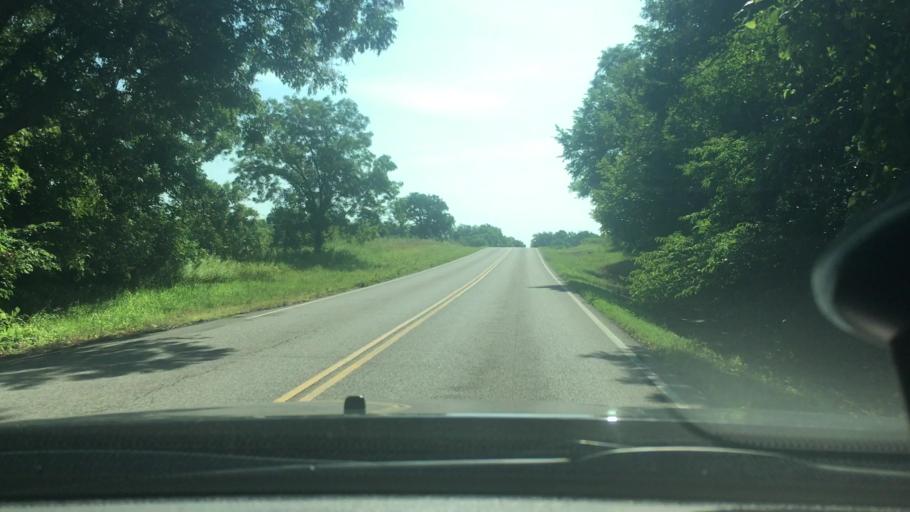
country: US
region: Oklahoma
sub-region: Garvin County
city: Pauls Valley
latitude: 34.6520
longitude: -97.3005
